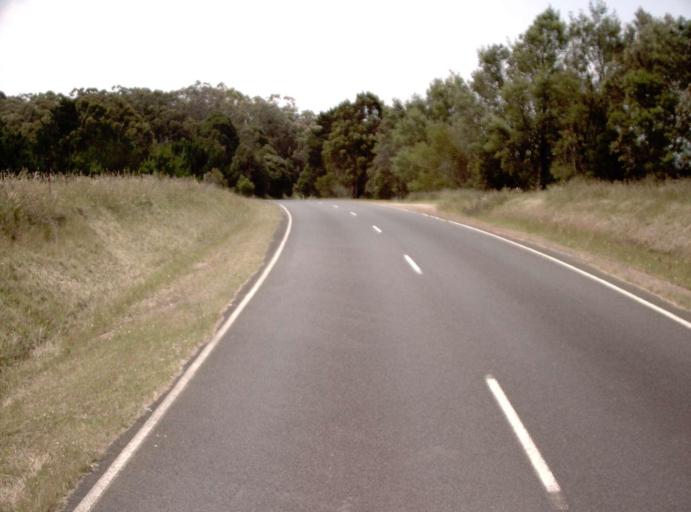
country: AU
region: Victoria
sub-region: Latrobe
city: Traralgon
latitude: -38.3556
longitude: 146.7096
